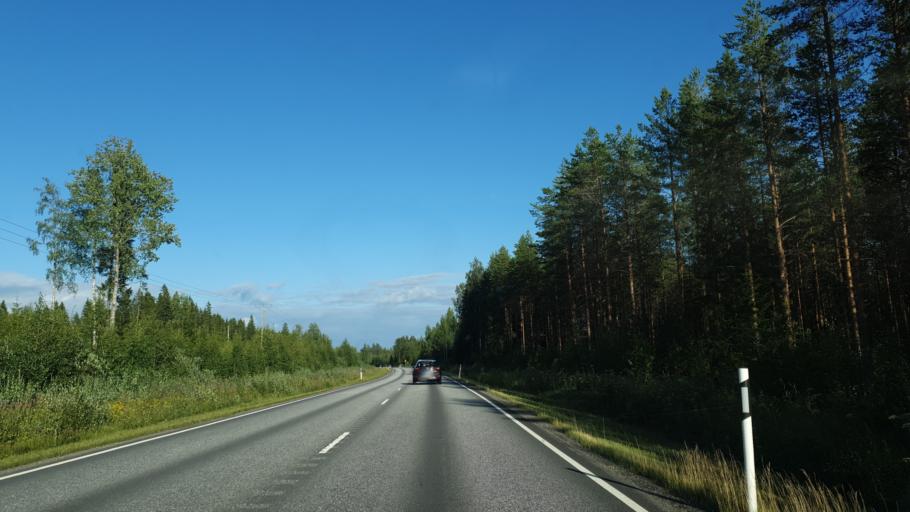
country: FI
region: North Karelia
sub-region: Joensuu
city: Outokumpu
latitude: 62.5337
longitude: 28.9557
